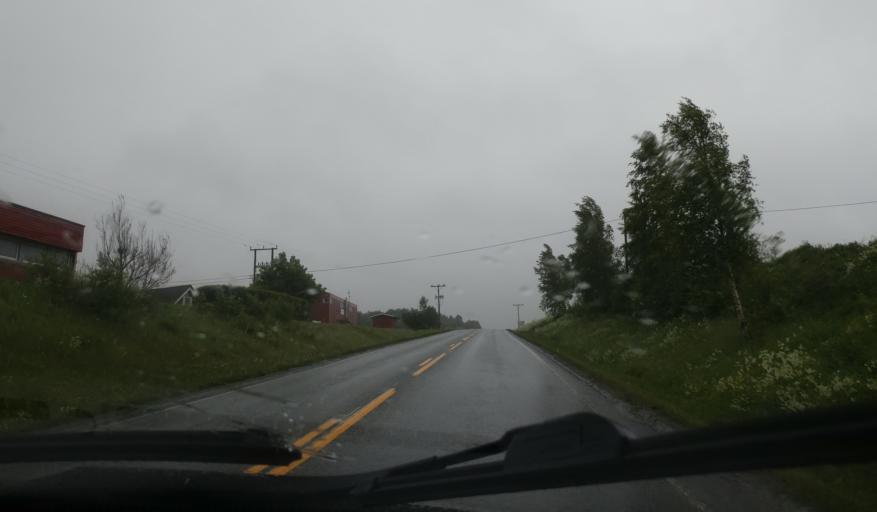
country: NO
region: Nord-Trondelag
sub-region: Stjordal
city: Stjordalshalsen
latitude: 63.4121
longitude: 10.9354
